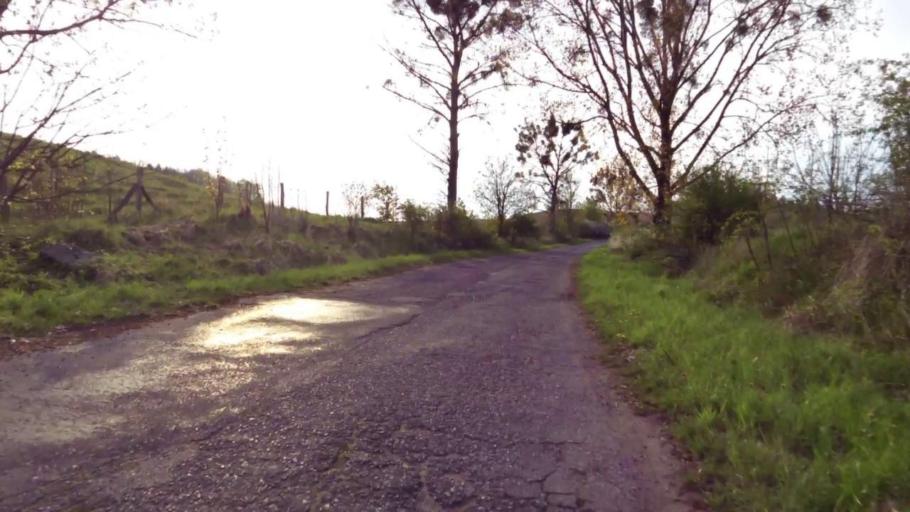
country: PL
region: West Pomeranian Voivodeship
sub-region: Powiat mysliborski
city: Mysliborz
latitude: 52.8947
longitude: 14.7775
